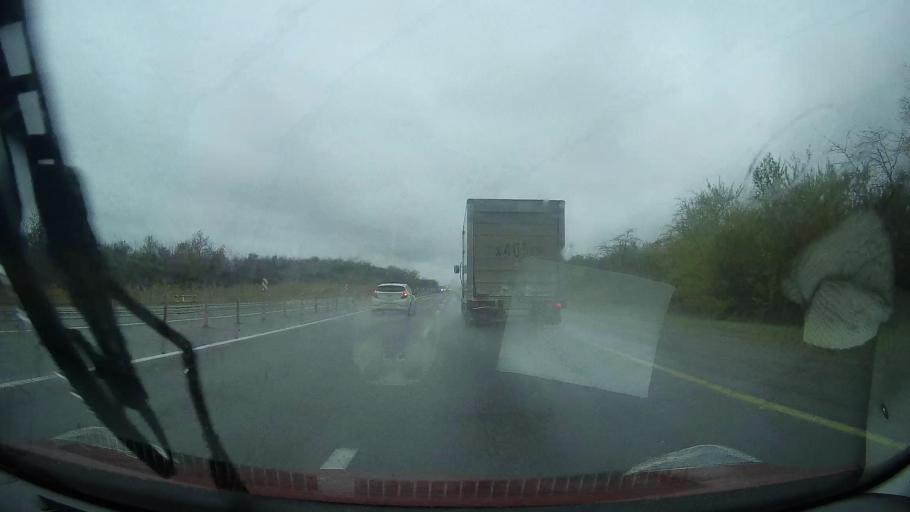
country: RU
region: Stavropol'skiy
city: Nevinnomyssk
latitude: 44.6382
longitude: 41.9831
